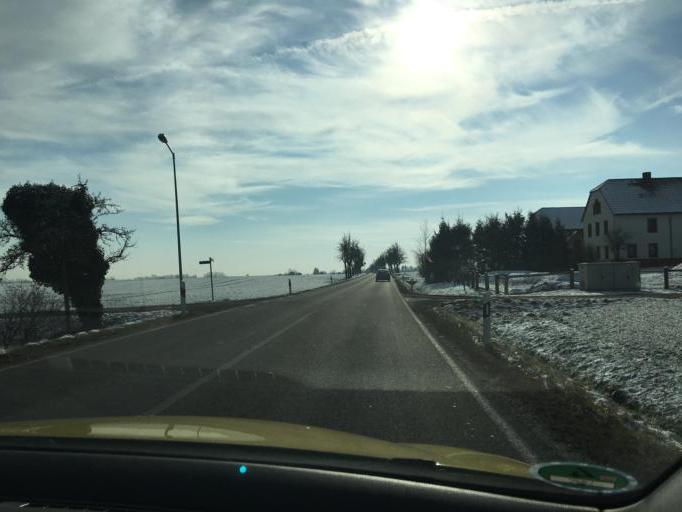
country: DE
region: Saxony
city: Narsdorf
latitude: 51.0255
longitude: 12.7281
